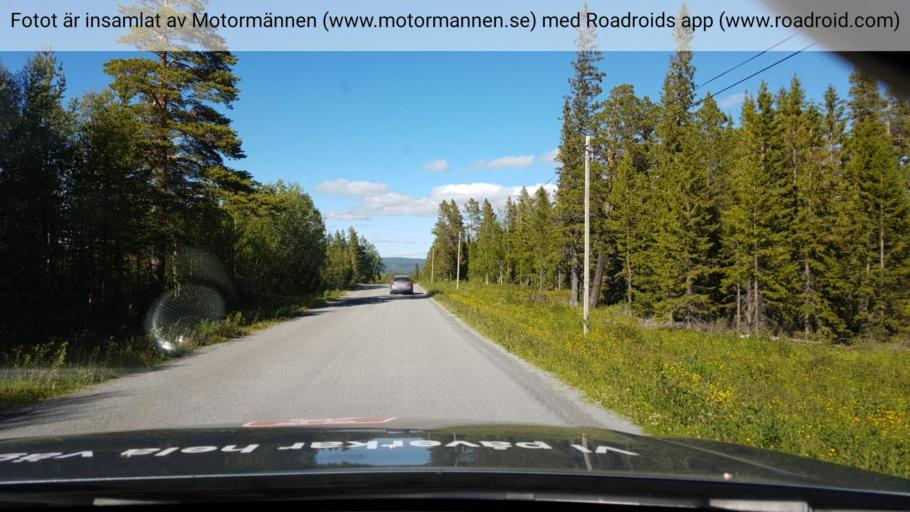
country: SE
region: Jaemtland
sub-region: Are Kommun
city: Are
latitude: 63.1657
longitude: 13.0761
